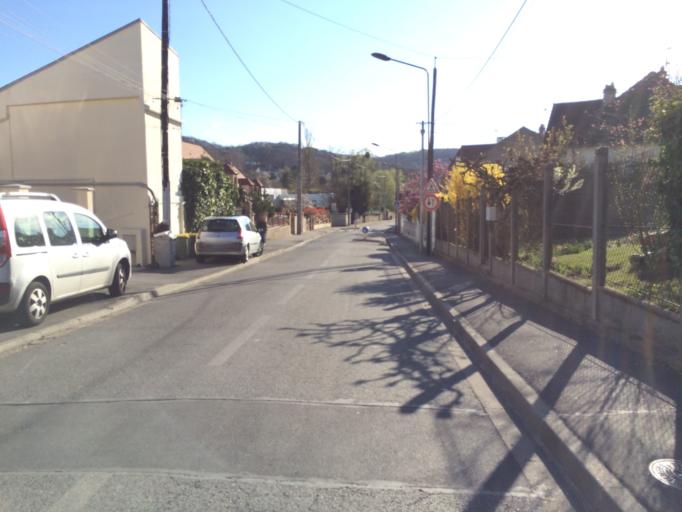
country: FR
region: Ile-de-France
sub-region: Departement de l'Essonne
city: Villebon-sur-Yvette
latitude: 48.7026
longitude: 2.2366
